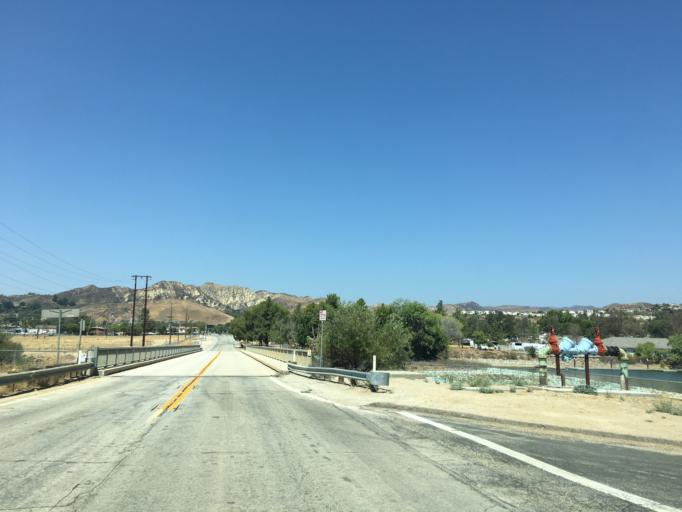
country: US
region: California
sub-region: Los Angeles County
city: Castaic
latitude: 34.4972
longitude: -118.6110
